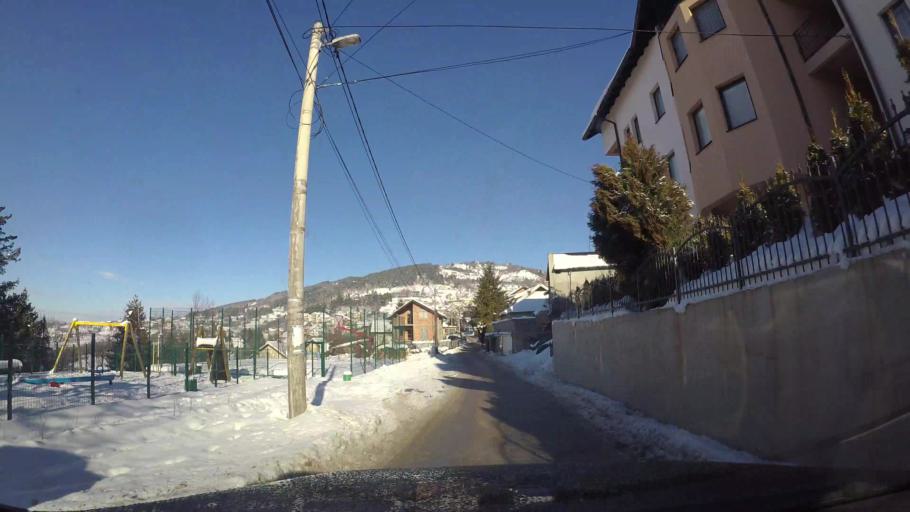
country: BA
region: Federation of Bosnia and Herzegovina
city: Kobilja Glava
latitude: 43.8898
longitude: 18.4091
